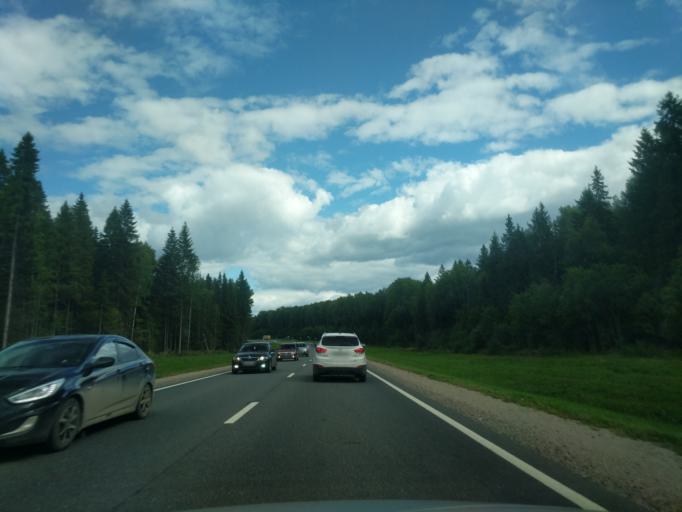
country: RU
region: Kostroma
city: Oktyabr'skiy
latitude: 57.7908
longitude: 41.1507
